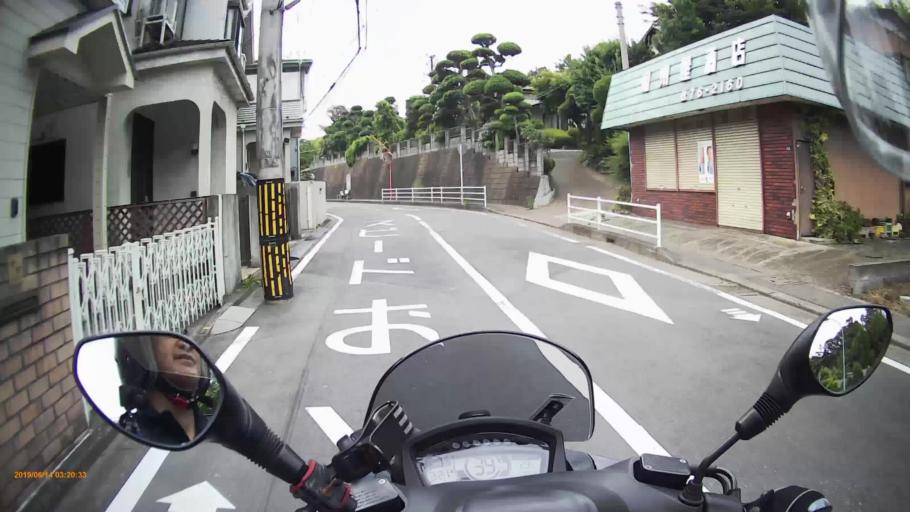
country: JP
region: Kanagawa
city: Minami-rinkan
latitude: 35.4131
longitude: 139.4529
